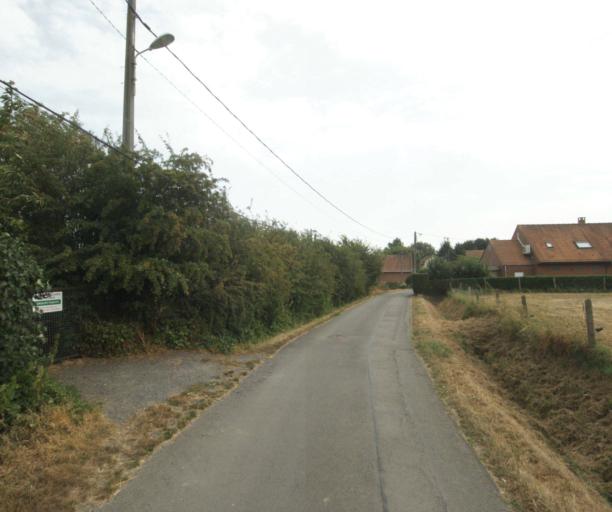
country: BE
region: Wallonia
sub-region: Province du Hainaut
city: Estaimpuis
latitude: 50.6981
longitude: 3.2564
